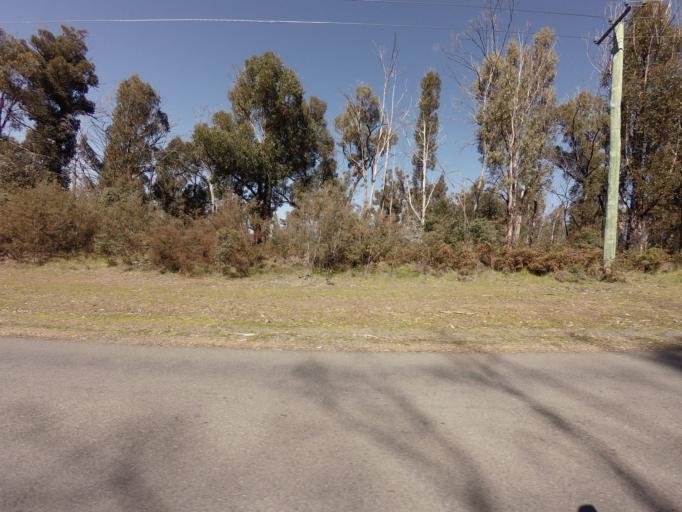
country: AU
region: Tasmania
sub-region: Derwent Valley
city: New Norfolk
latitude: -42.5528
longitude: 146.7131
